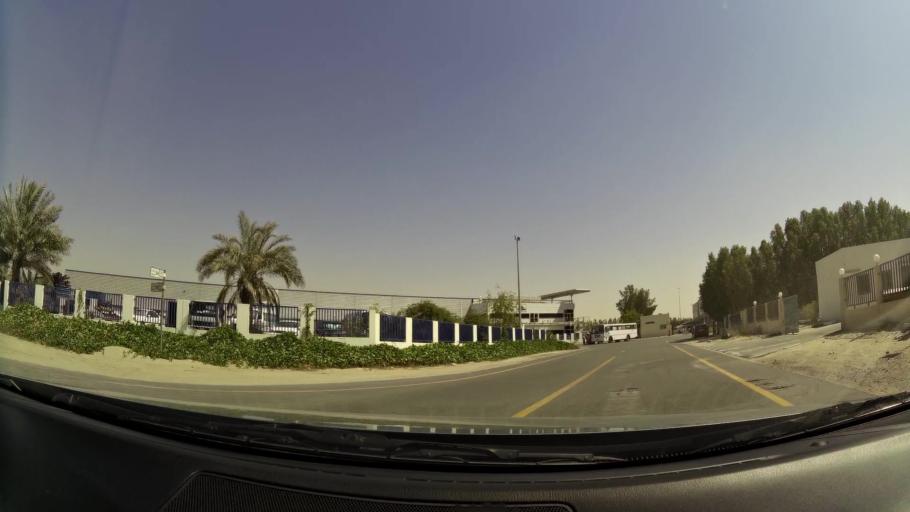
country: AE
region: Dubai
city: Dubai
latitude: 24.9677
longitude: 55.1782
